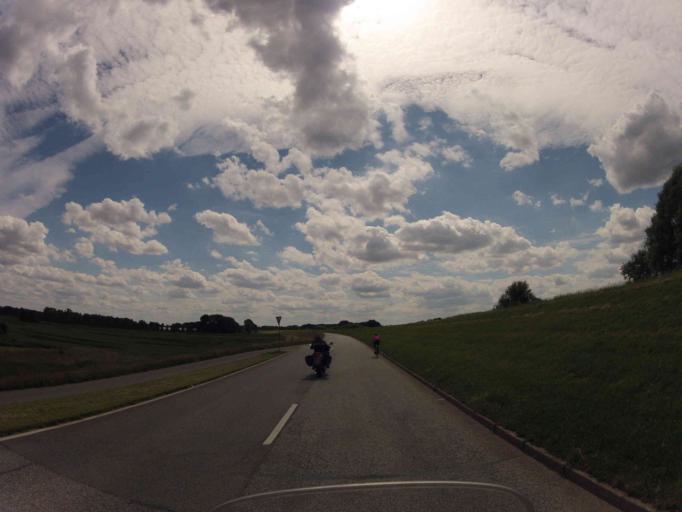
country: DE
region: Hamburg
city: Rothenburgsort
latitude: 53.4986
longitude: 10.0550
